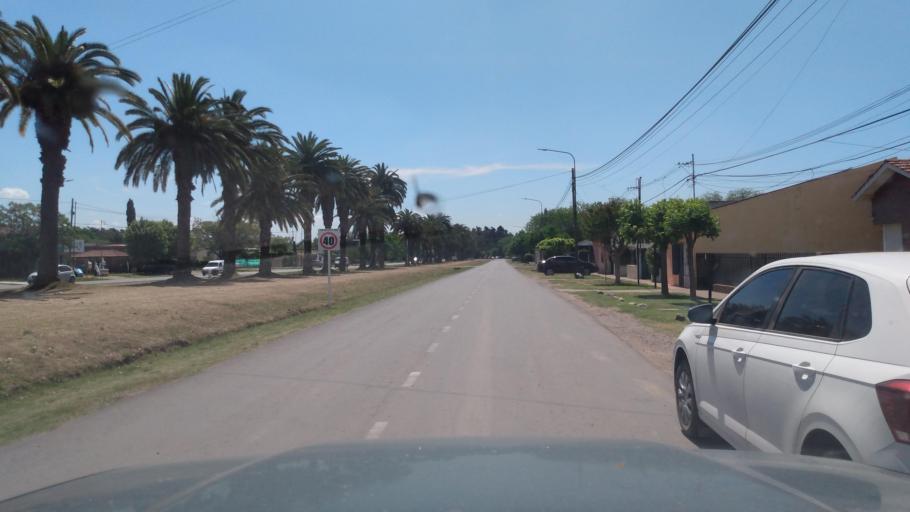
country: AR
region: Buenos Aires
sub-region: Partido de Lujan
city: Lujan
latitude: -34.5966
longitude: -59.1766
